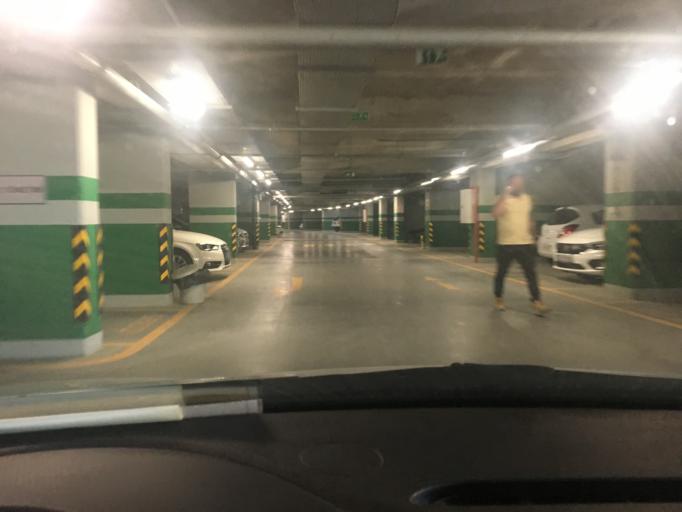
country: TR
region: Istanbul
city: Sisli
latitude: 41.0906
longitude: 28.9464
